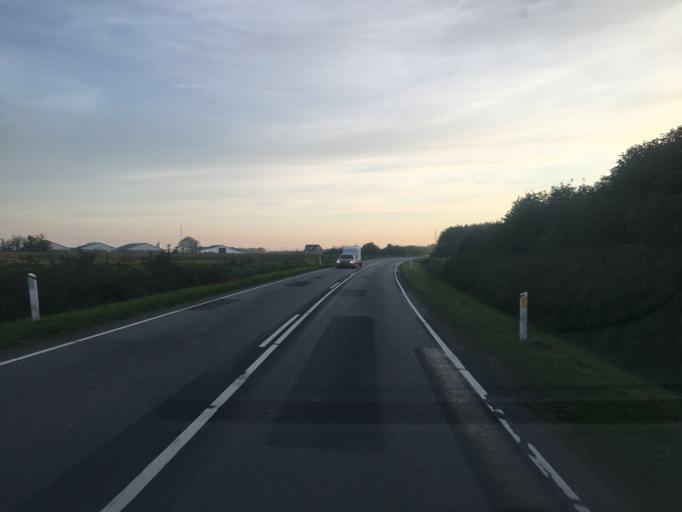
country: DK
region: South Denmark
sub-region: Tonder Kommune
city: Logumkloster
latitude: 55.0467
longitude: 9.0930
